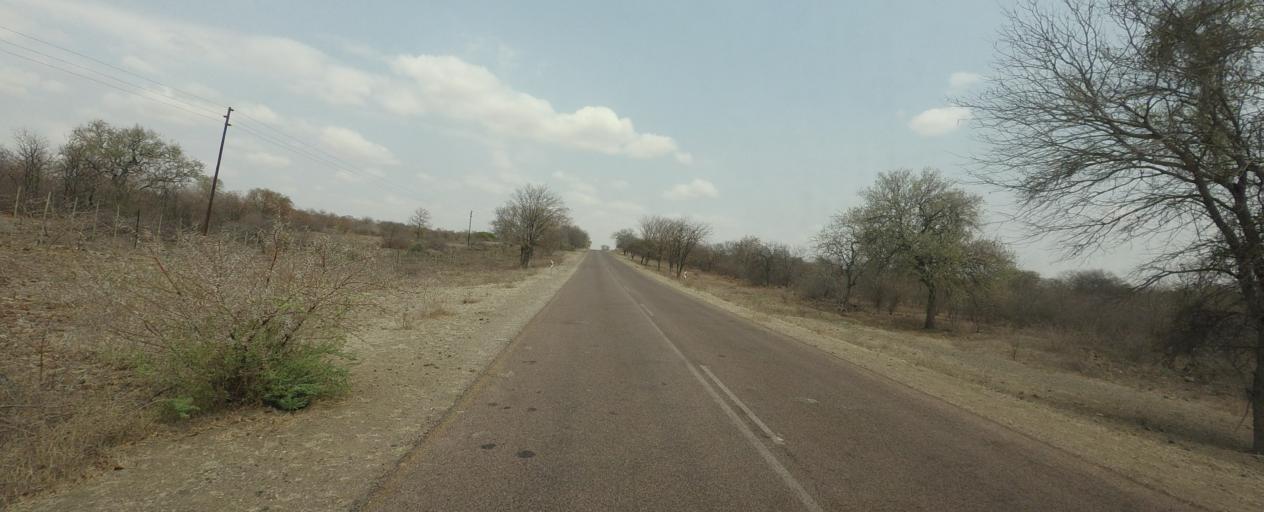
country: ZA
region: Limpopo
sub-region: Vhembe District Municipality
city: Mutale
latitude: -22.4194
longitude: 30.9680
